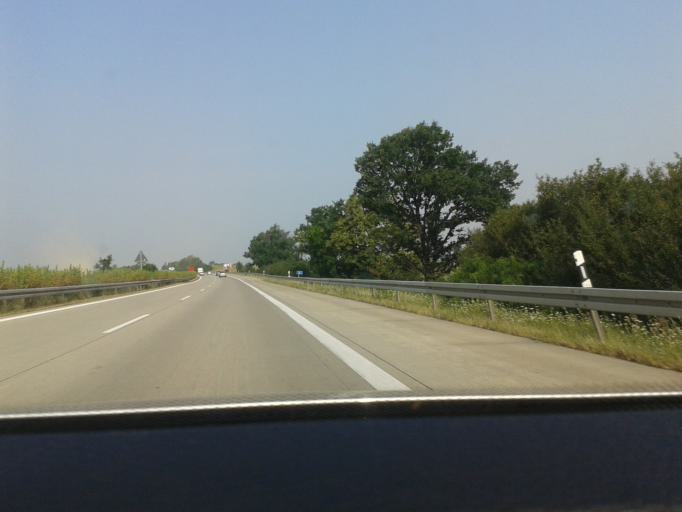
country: DE
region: Saxony
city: Rosswein
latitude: 51.0993
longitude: 13.2105
